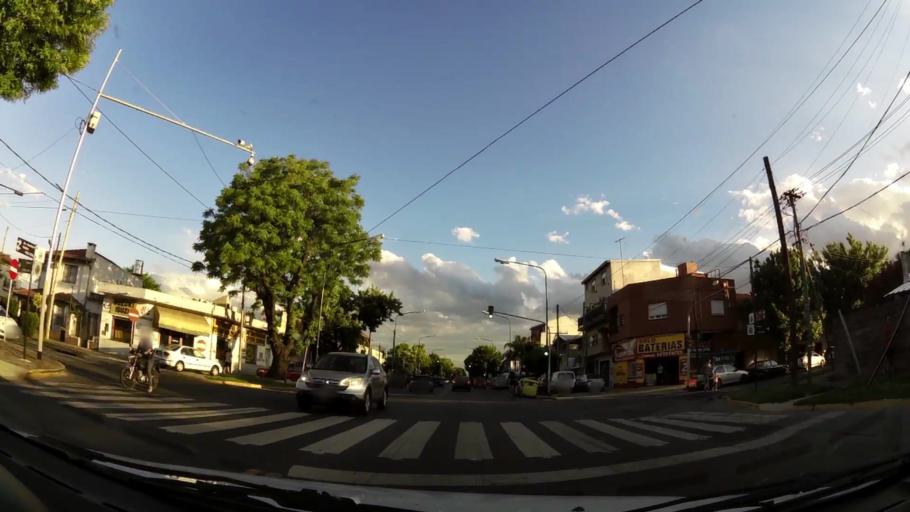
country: AR
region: Buenos Aires
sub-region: Partido de San Isidro
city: San Isidro
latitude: -34.4790
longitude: -58.5291
